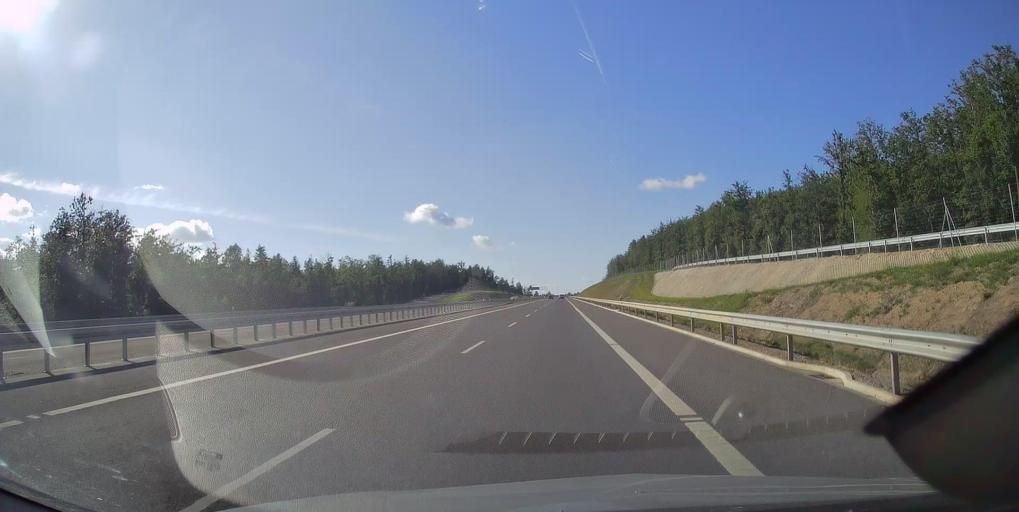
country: PL
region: Swietokrzyskie
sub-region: Powiat skarzyski
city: Skarzysko-Kamienna
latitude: 51.1272
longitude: 20.8413
